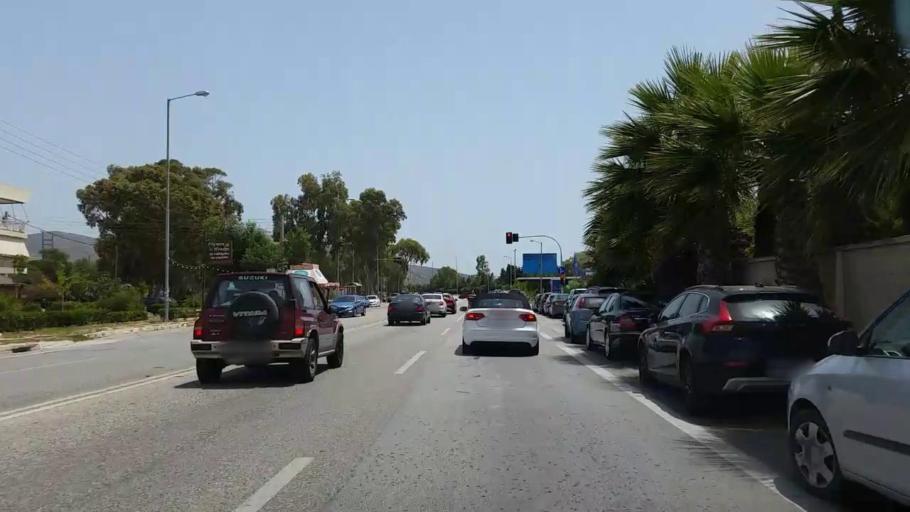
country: GR
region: Attica
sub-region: Nomarchia Anatolikis Attikis
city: Saronida
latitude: 37.7819
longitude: 23.8901
